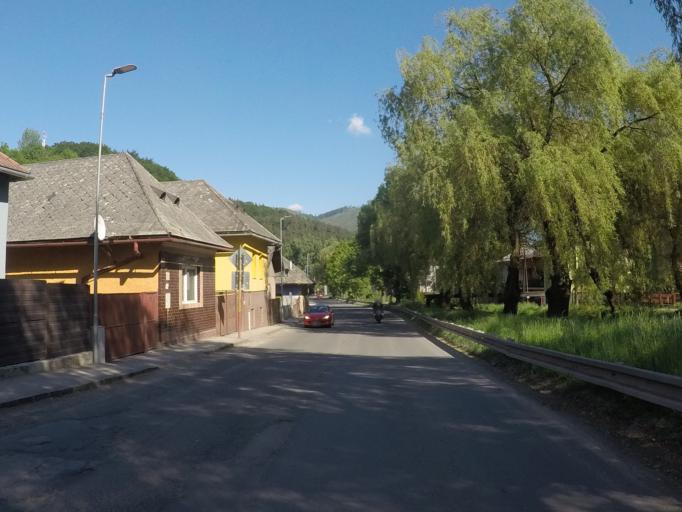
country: SK
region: Kosicky
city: Dobsina
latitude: 48.8194
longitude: 20.3753
